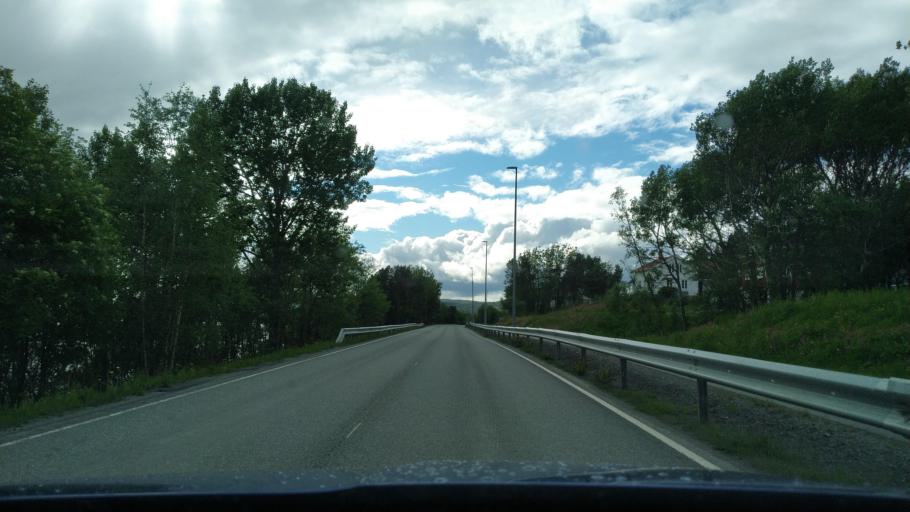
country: NO
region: Troms
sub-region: Sorreisa
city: Sorreisa
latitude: 69.1775
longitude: 18.0784
